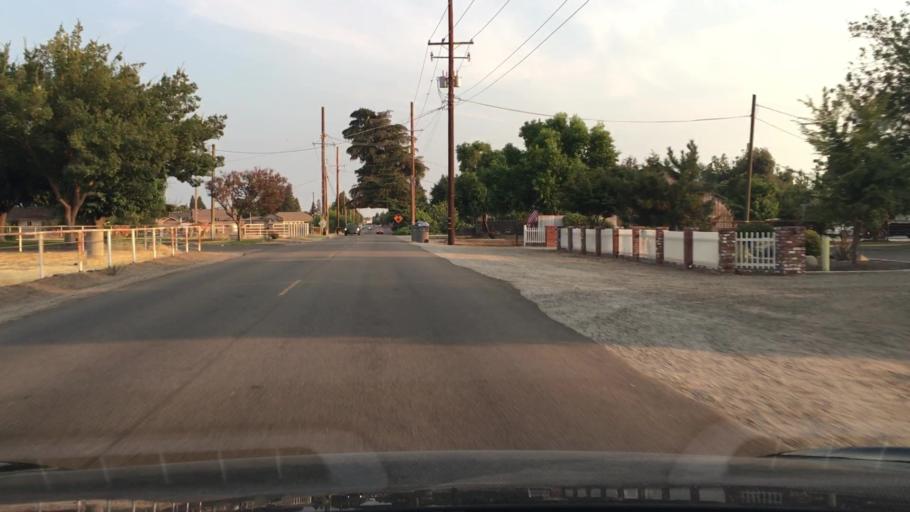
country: US
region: California
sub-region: Fresno County
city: Clovis
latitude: 36.8546
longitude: -119.6931
